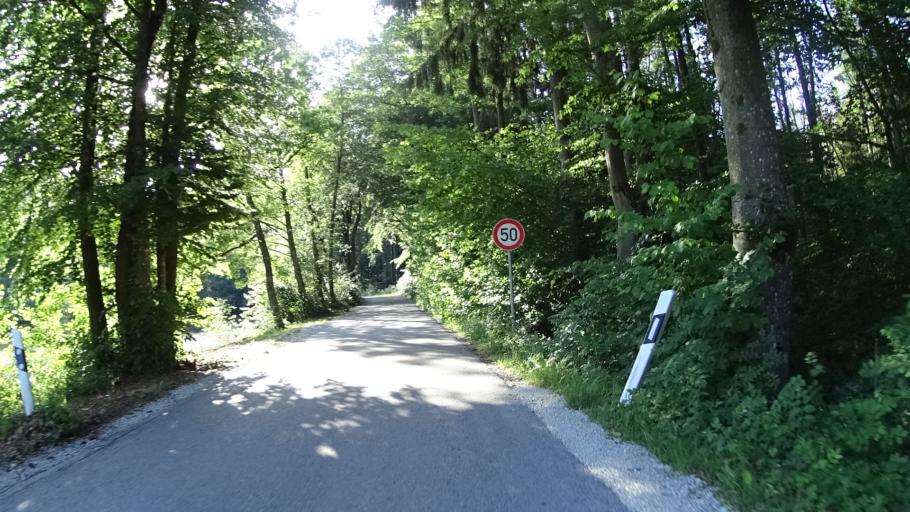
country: DE
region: Bavaria
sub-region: Regierungsbezirk Mittelfranken
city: Lichtenau
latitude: 49.1505
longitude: 10.3931
